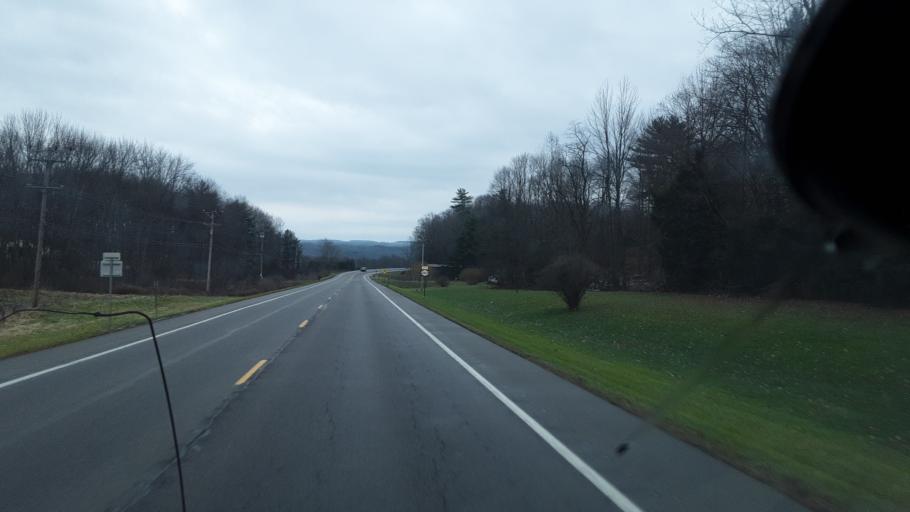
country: US
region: New York
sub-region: Allegany County
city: Houghton
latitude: 42.3933
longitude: -78.1782
